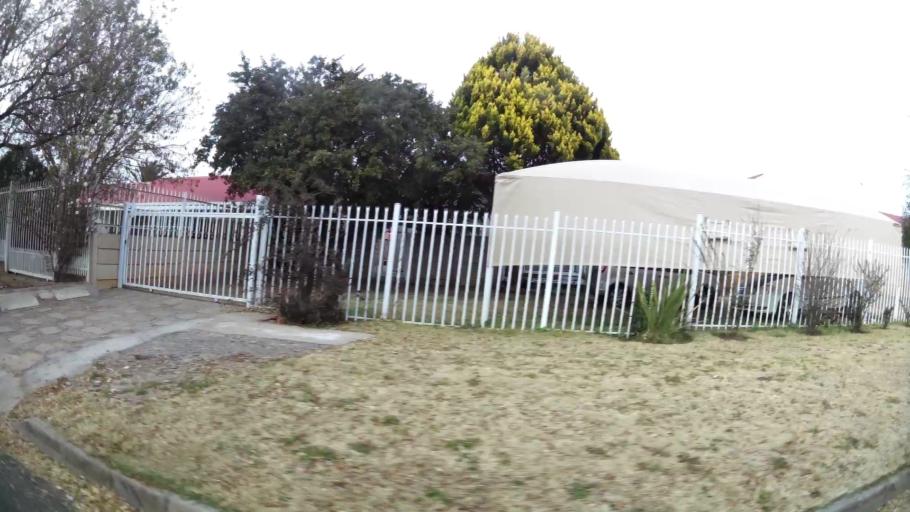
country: ZA
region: Orange Free State
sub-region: Mangaung Metropolitan Municipality
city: Bloemfontein
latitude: -29.1251
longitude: 26.1829
